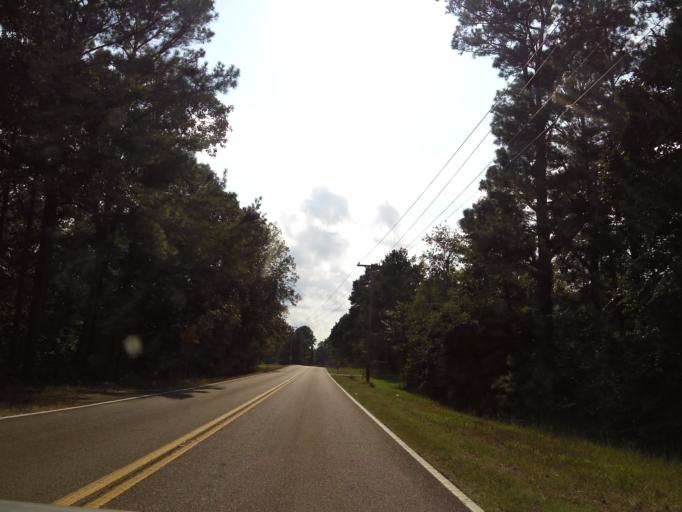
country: US
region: Tennessee
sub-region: Hardin County
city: Crump
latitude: 35.1064
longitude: -88.3727
